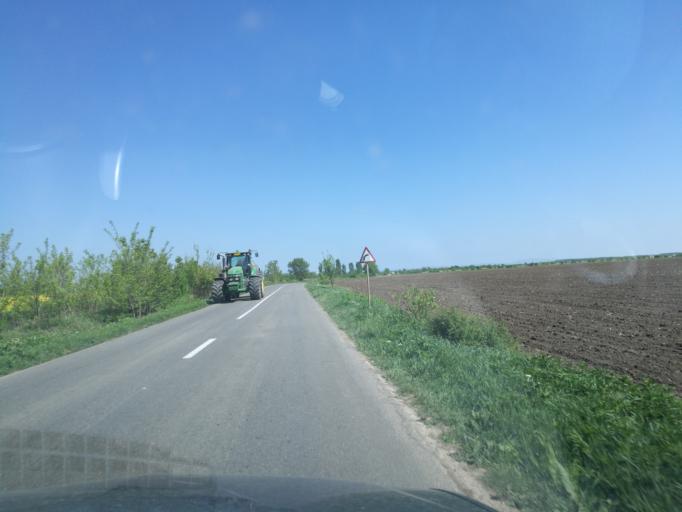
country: RO
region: Prahova
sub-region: Comuna Gherghita
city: Gherghita
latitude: 44.7840
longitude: 26.2620
